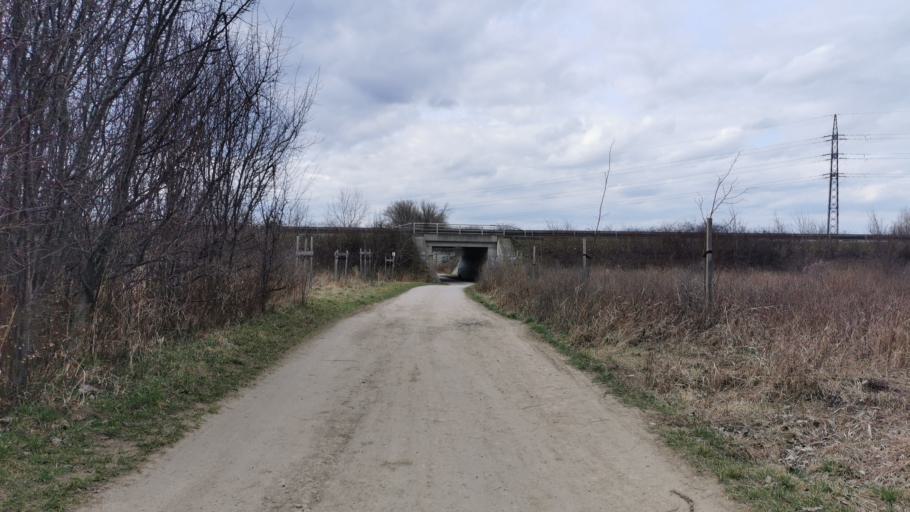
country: SK
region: Trnavsky
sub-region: Okres Skalica
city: Skalica
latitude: 48.8560
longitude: 17.2269
